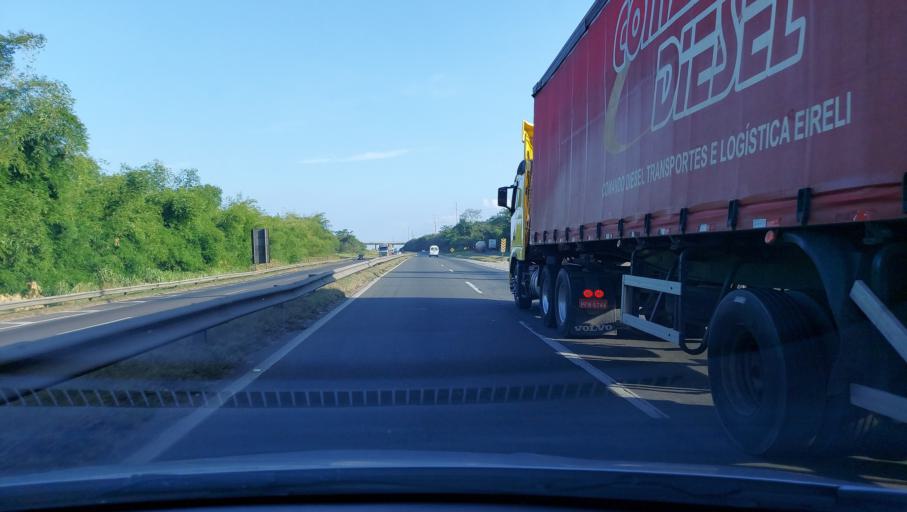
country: BR
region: Bahia
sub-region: Conceicao Do Jacuipe
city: Conceicao do Jacuipe
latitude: -12.3564
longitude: -38.8291
